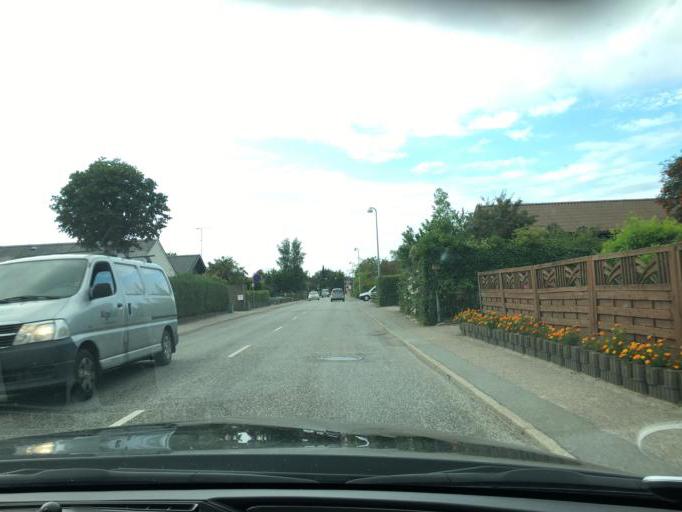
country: DK
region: Capital Region
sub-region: Gribskov Kommune
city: Helsinge
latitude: 56.0177
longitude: 12.1980
